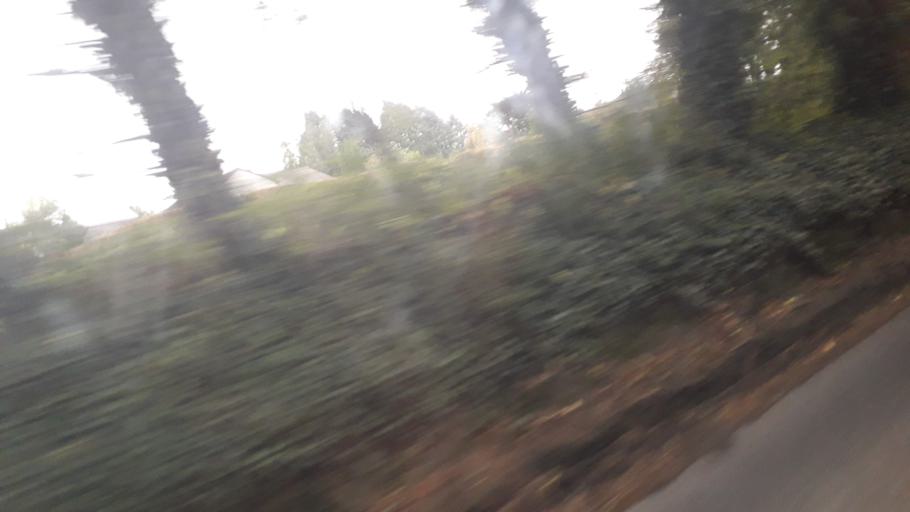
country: IE
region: Munster
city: Ballina
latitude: 52.7960
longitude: -8.4347
